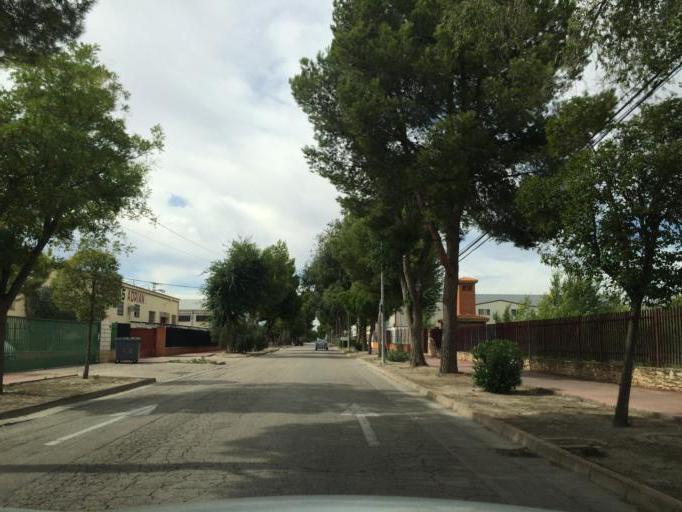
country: ES
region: Castille-La Mancha
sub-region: Provincia de Albacete
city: Albacete
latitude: 39.0136
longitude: -1.8806
